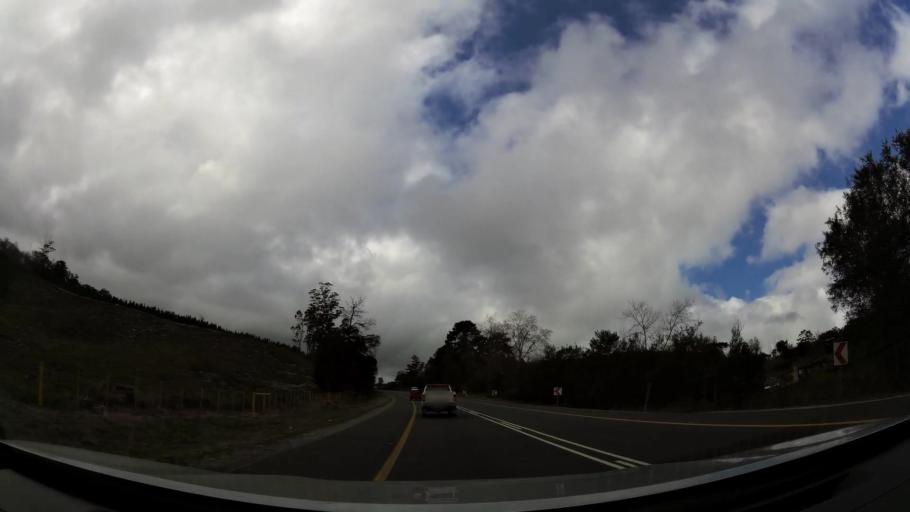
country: ZA
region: Western Cape
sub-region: Eden District Municipality
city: Knysna
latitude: -34.0273
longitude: 23.1721
